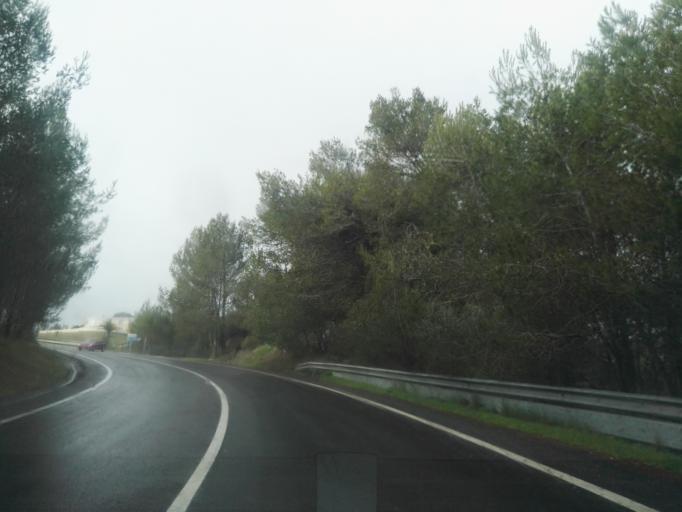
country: PT
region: Lisbon
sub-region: Vila Franca de Xira
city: Sobralinho
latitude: 38.9032
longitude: -9.0553
